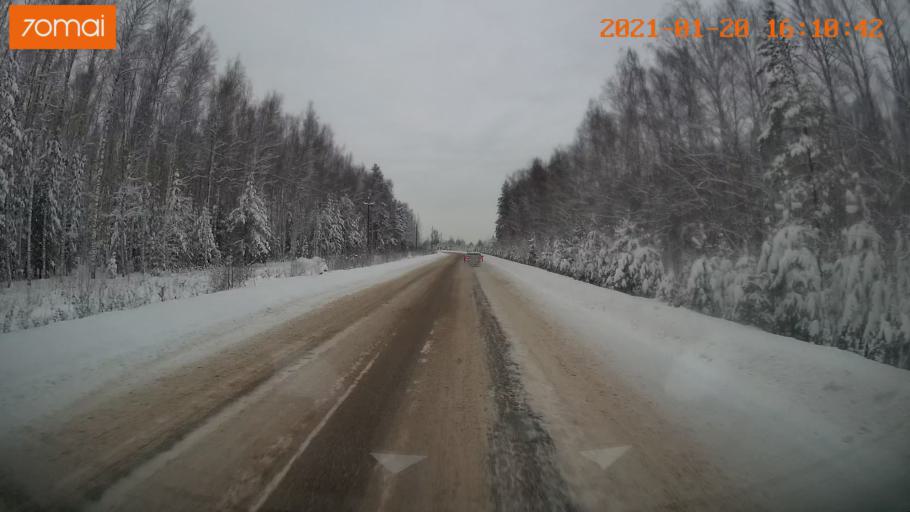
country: RU
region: Vladimir
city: Sudogda
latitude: 56.0947
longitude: 40.7859
